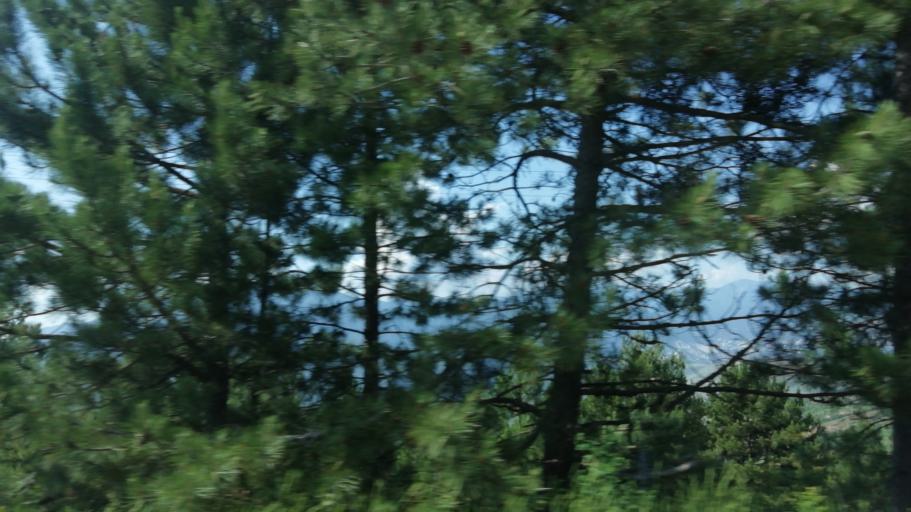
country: TR
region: Karabuk
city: Karabuk
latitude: 41.1248
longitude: 32.5864
